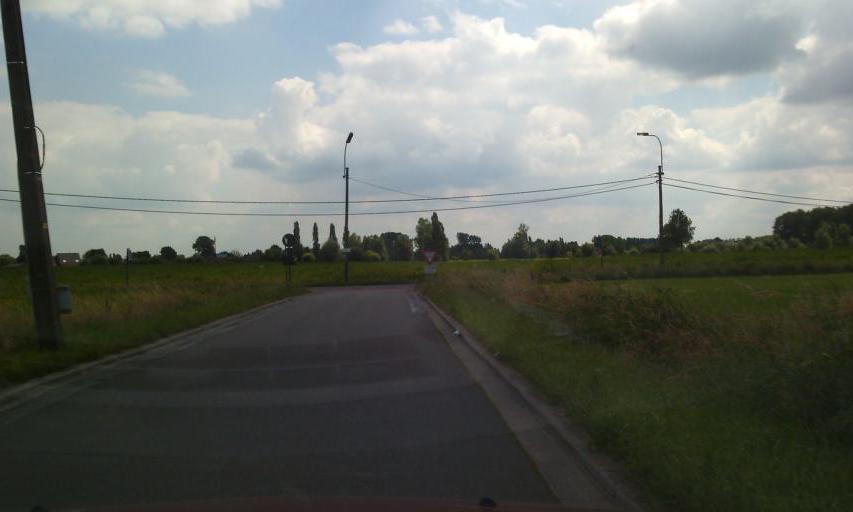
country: BE
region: Flanders
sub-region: Provincie Oost-Vlaanderen
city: Lochristi
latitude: 51.0838
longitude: 3.9107
